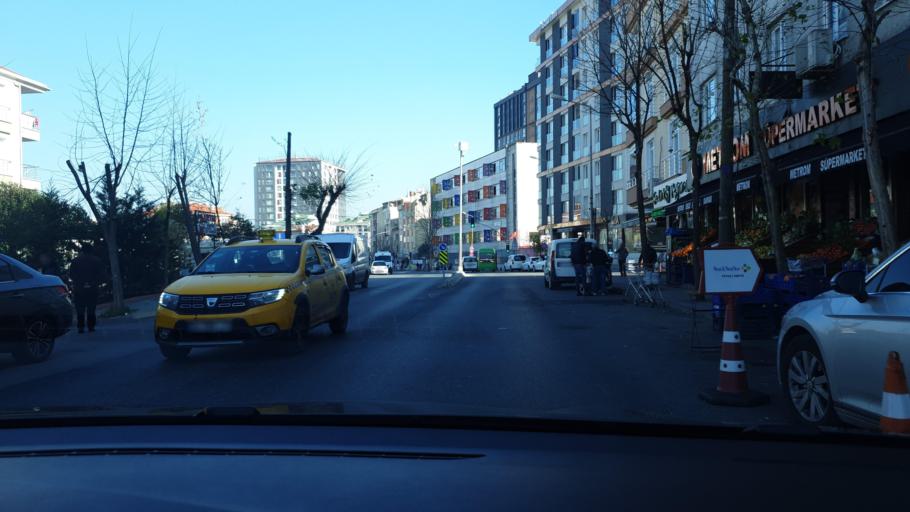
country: TR
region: Istanbul
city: Sisli
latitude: 41.0786
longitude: 28.9622
